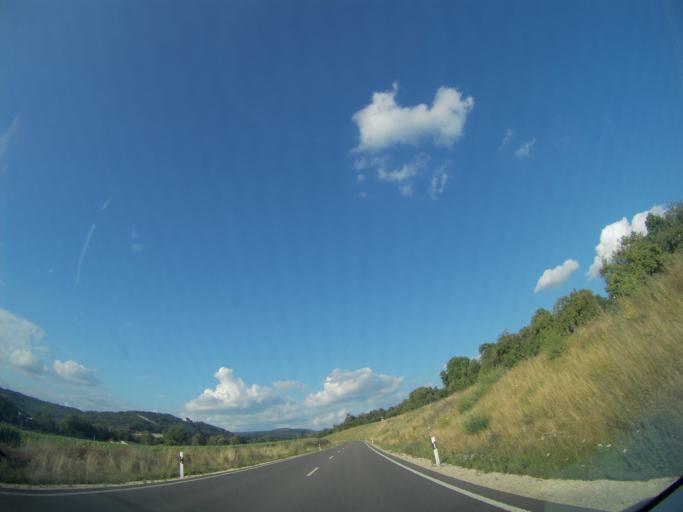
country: DE
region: Baden-Wuerttemberg
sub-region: Regierungsbezirk Stuttgart
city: Sussen
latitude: 48.6797
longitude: 9.7717
